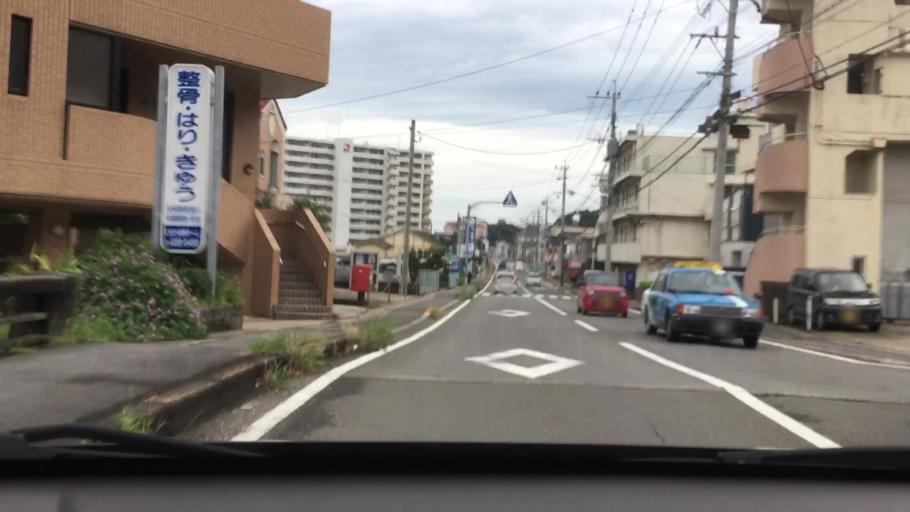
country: JP
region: Nagasaki
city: Nagasaki-shi
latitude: 32.7584
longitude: 129.9428
